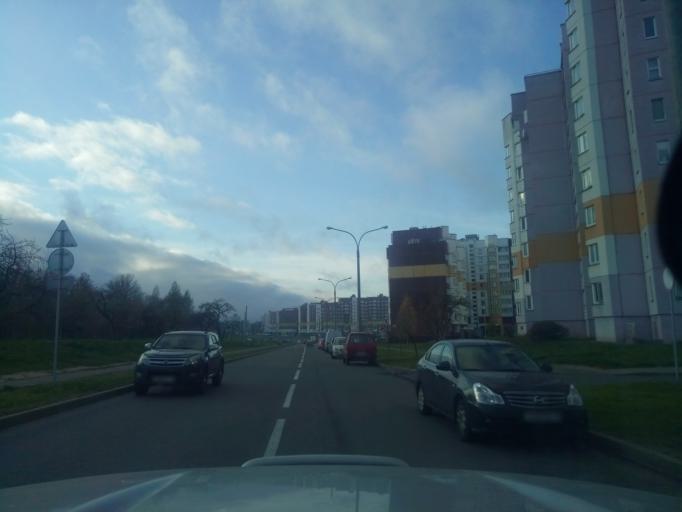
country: BY
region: Minsk
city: Novoye Medvezhino
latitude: 53.8769
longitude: 27.4842
